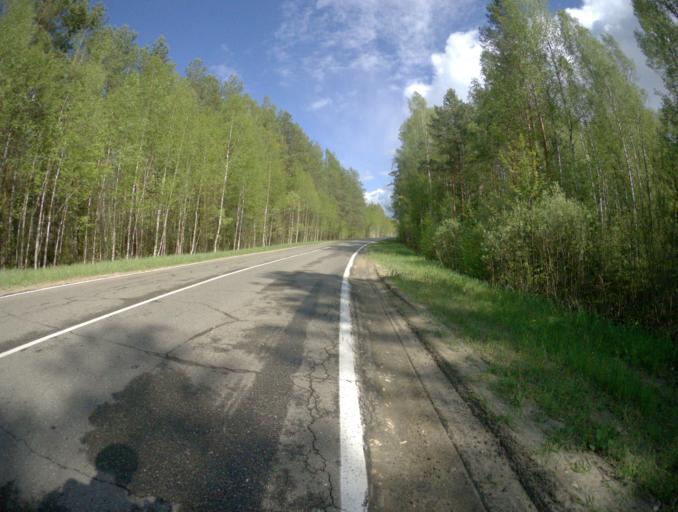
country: RU
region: Vladimir
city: Urshel'skiy
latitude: 55.6088
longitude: 40.2719
